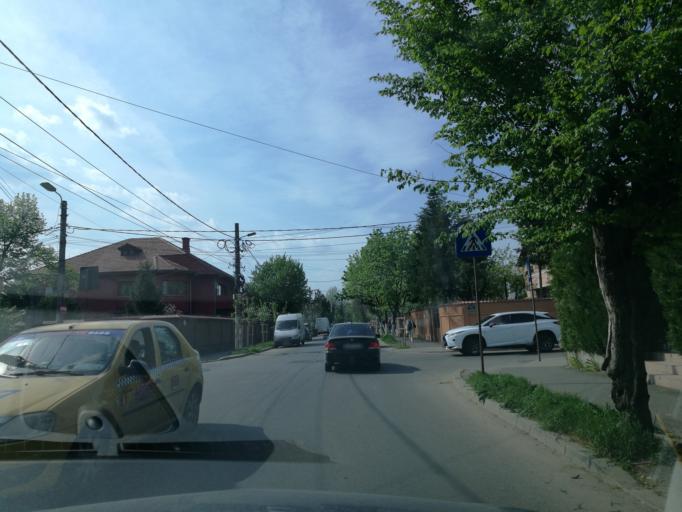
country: RO
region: Ilfov
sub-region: Comuna Chiajna
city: Rosu
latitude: 44.4425
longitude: 26.0299
